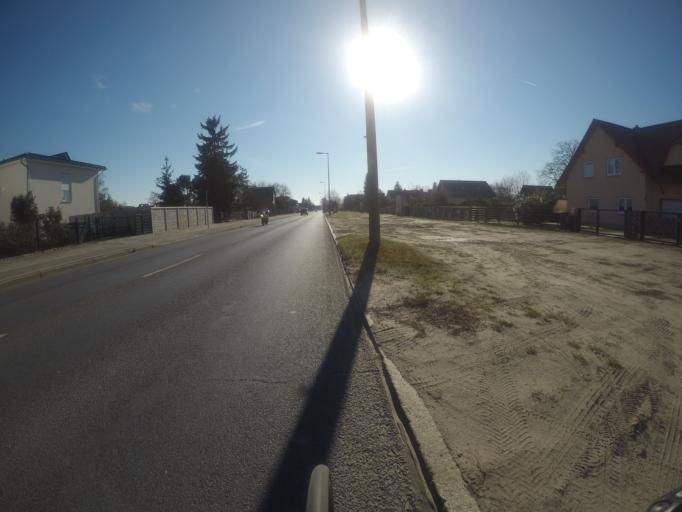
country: DE
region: Berlin
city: Kaulsdorf
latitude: 52.4950
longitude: 13.5767
